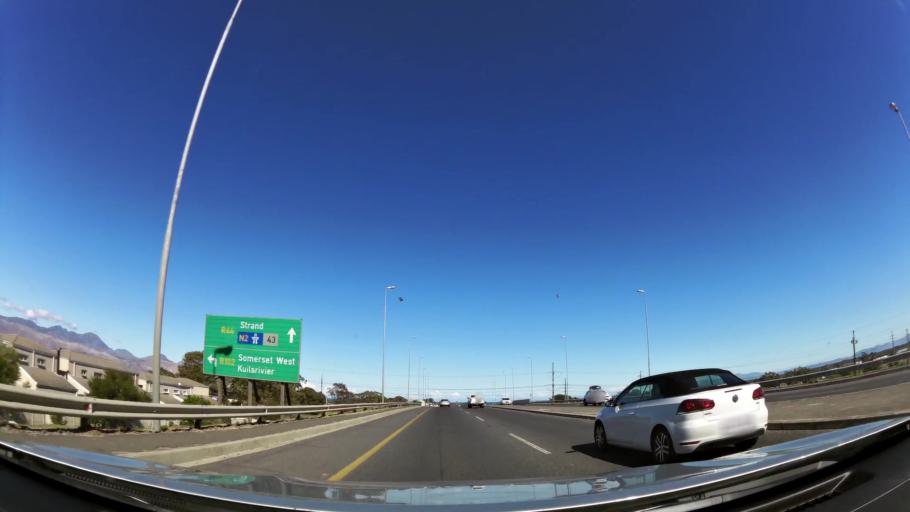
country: ZA
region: Western Cape
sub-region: Cape Winelands District Municipality
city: Stellenbosch
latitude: -34.0737
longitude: 18.8232
